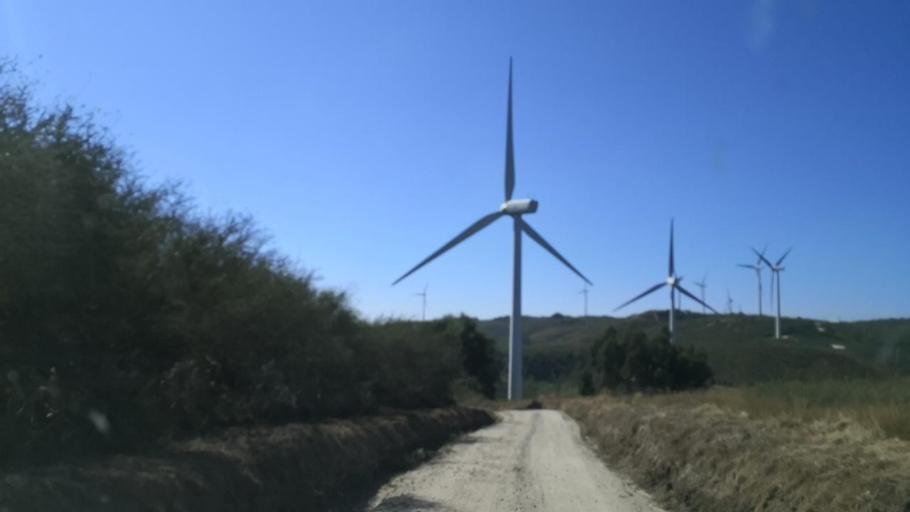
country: PT
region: Braga
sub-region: Cabeceiras de Basto
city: Refojos de Basto
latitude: 41.4967
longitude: -8.0723
